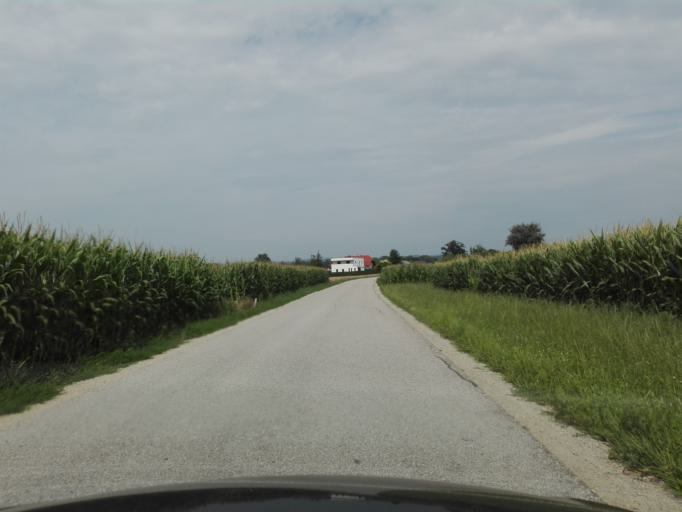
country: AT
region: Lower Austria
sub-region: Politischer Bezirk Amstetten
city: Strengberg
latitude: 48.1856
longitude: 14.6880
